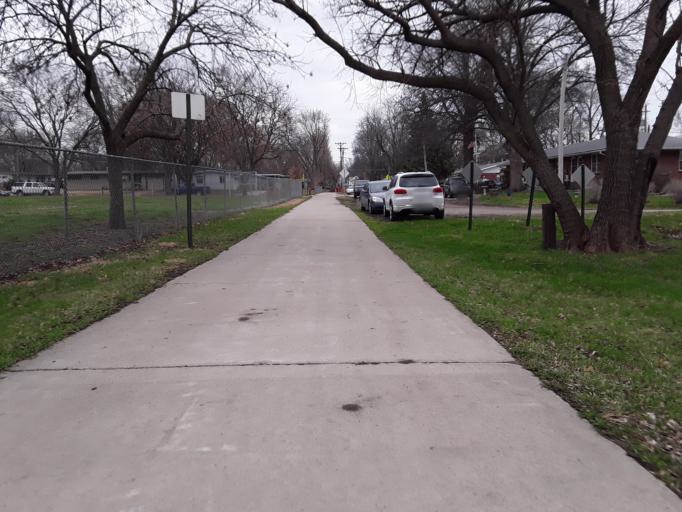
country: US
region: Nebraska
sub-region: Lancaster County
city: Lincoln
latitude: 40.8509
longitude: -96.6523
